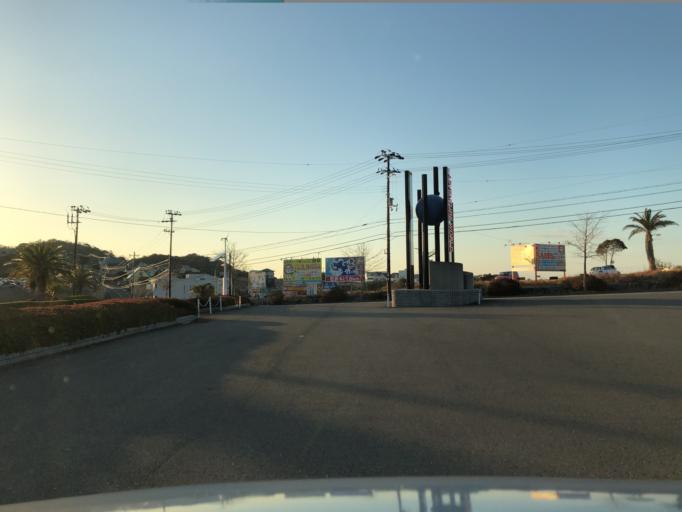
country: JP
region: Wakayama
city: Tanabe
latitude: 33.6698
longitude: 135.3741
